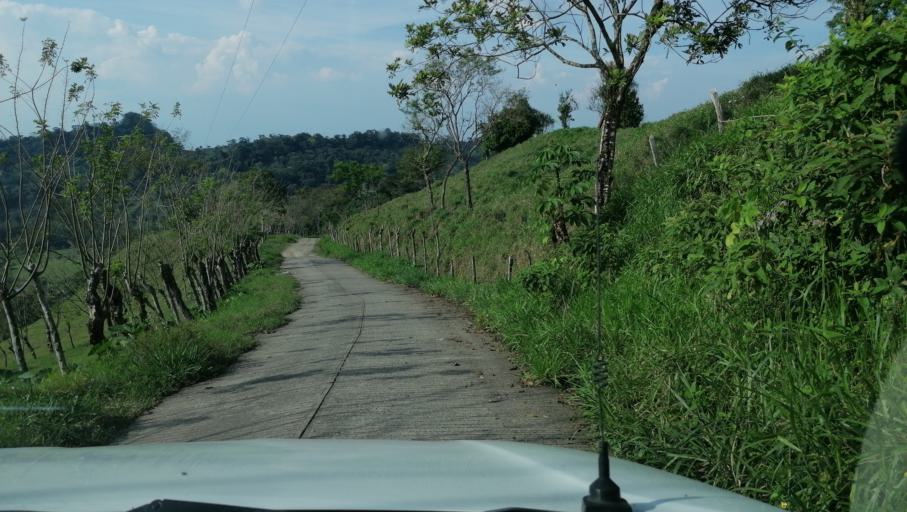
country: MX
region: Chiapas
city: Ostuacan
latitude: 17.4656
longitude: -93.2336
